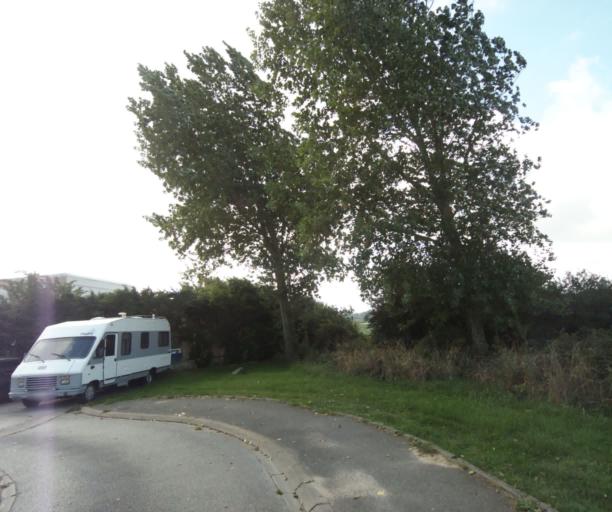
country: FR
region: Nord-Pas-de-Calais
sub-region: Departement du Pas-de-Calais
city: Etaples
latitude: 50.5242
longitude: 1.6257
